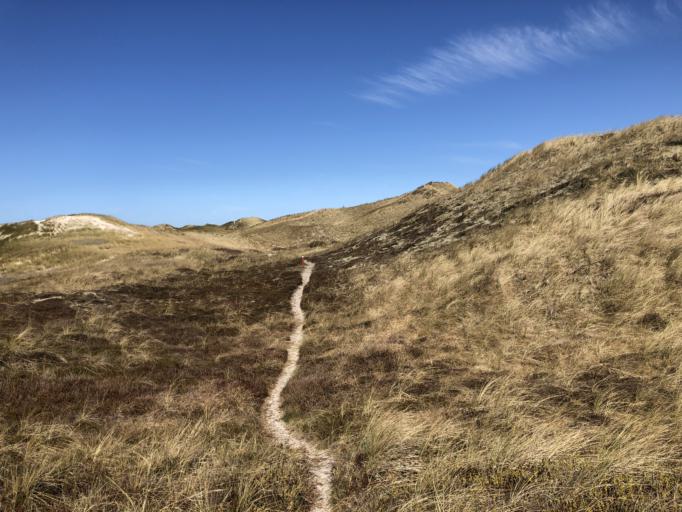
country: DK
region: Central Jutland
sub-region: Holstebro Kommune
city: Ulfborg
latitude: 56.3073
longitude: 8.1261
